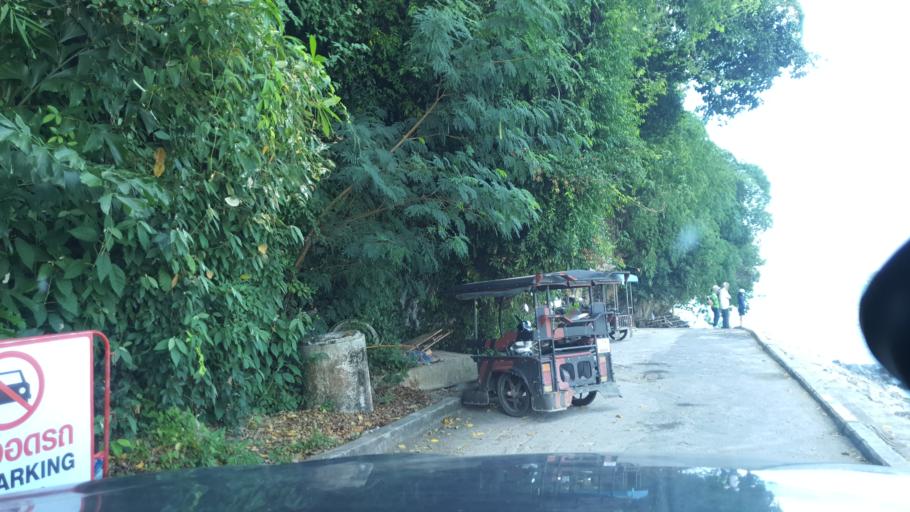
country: TH
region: Phangnga
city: Ban Ao Nang
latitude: 8.0377
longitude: 98.8156
